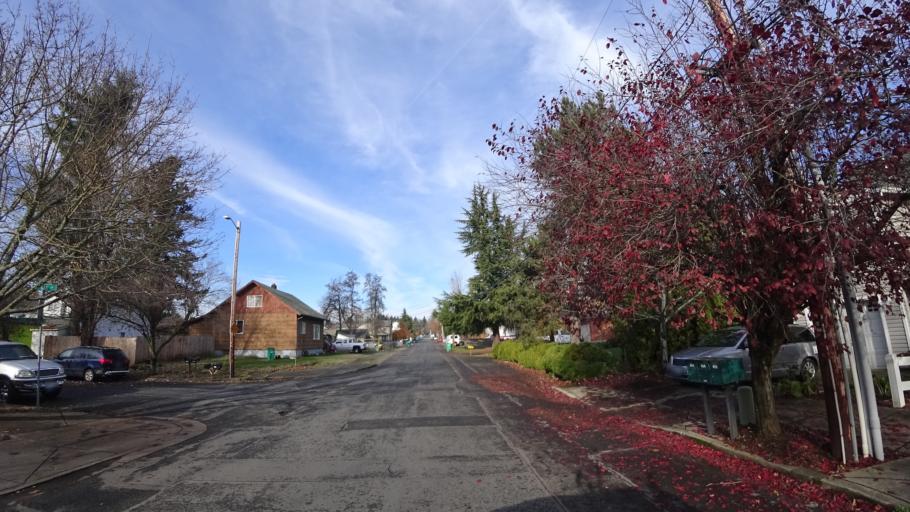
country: US
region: Oregon
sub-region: Multnomah County
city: Lents
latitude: 45.5199
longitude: -122.5159
